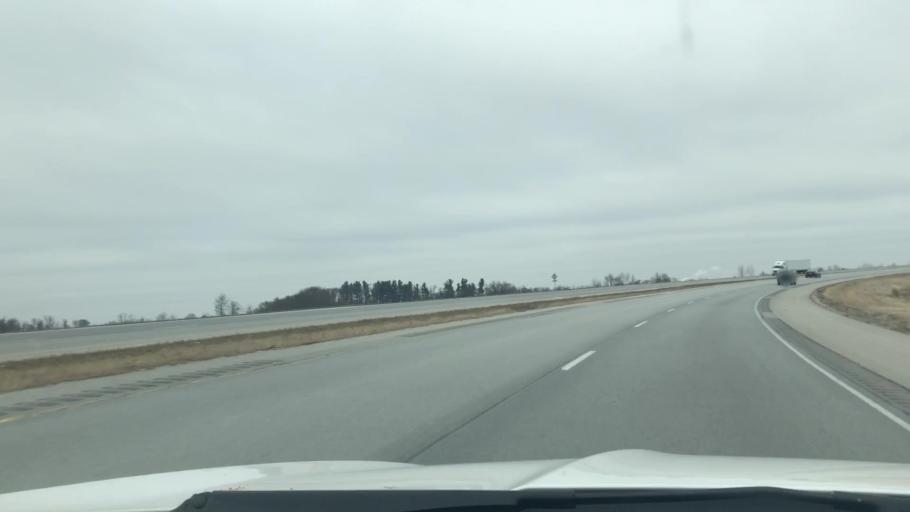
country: US
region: Indiana
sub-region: Cass County
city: Georgetown
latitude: 40.7082
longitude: -86.4545
